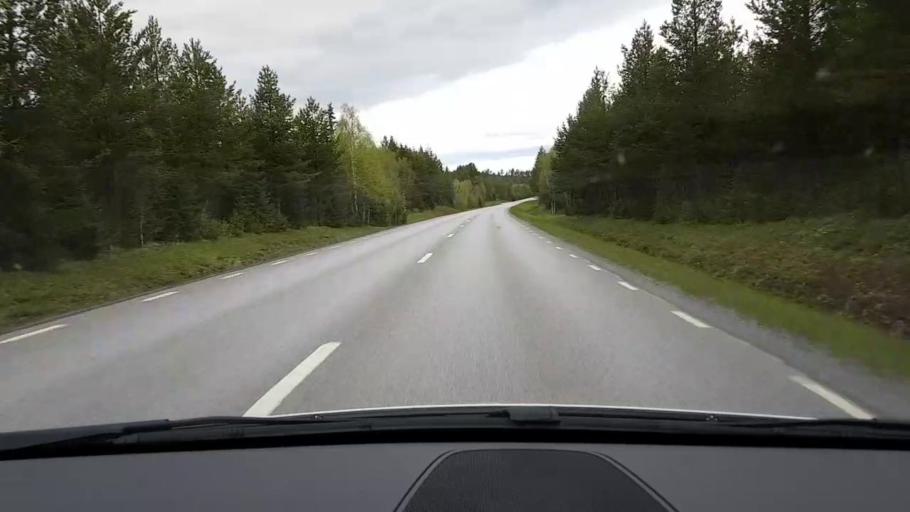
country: SE
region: Jaemtland
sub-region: Krokoms Kommun
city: Valla
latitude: 63.2890
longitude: 13.9276
